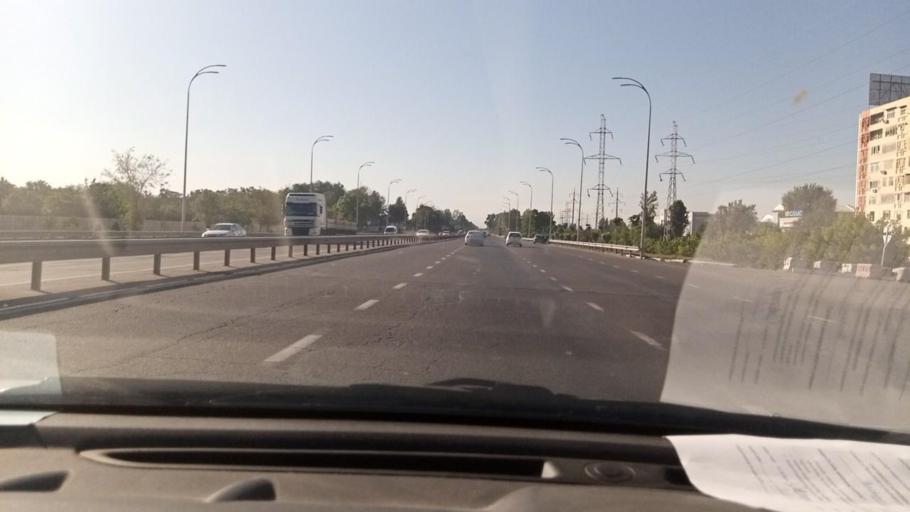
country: UZ
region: Toshkent Shahri
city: Bektemir
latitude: 41.2567
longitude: 69.3805
